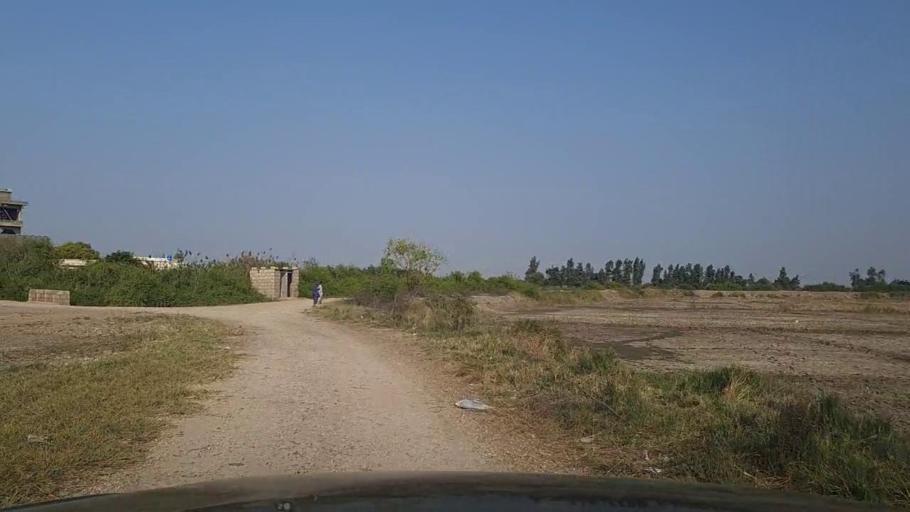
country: PK
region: Sindh
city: Mirpur Sakro
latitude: 24.6239
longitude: 67.7546
